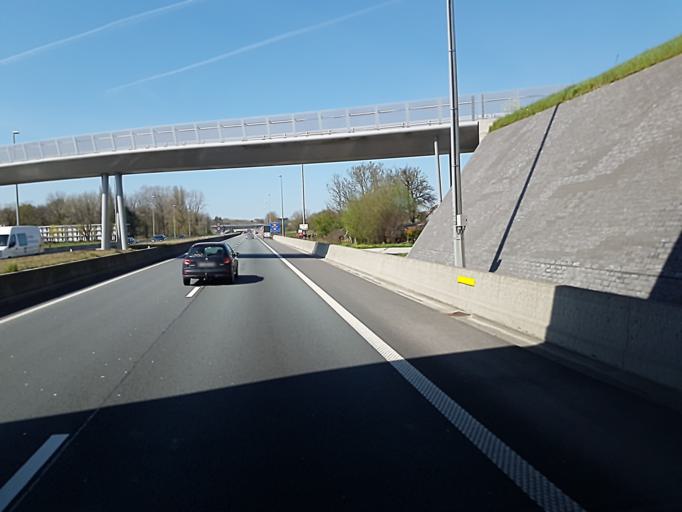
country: BE
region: Flanders
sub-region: Provincie West-Vlaanderen
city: Oostkamp
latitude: 51.1713
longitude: 3.2072
